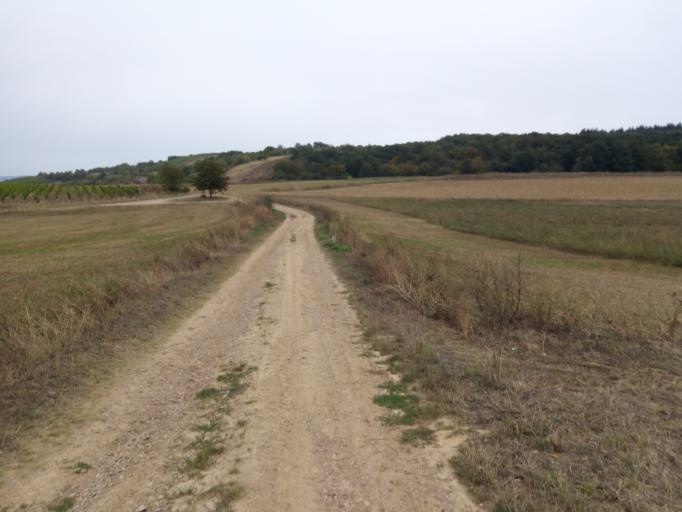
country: DE
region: Rheinland-Pfalz
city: Rummelsheim
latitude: 49.9237
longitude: 7.8518
